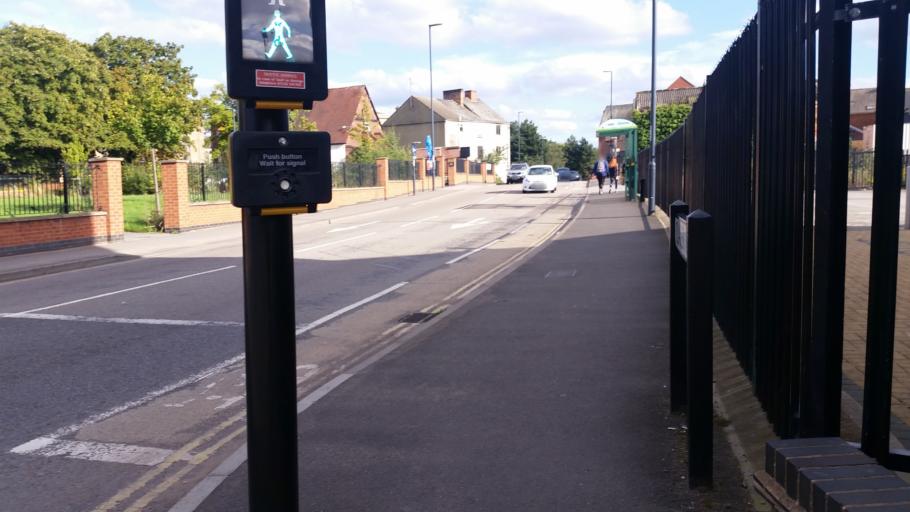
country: GB
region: England
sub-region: Derby
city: Derby
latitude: 52.9278
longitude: -1.4821
